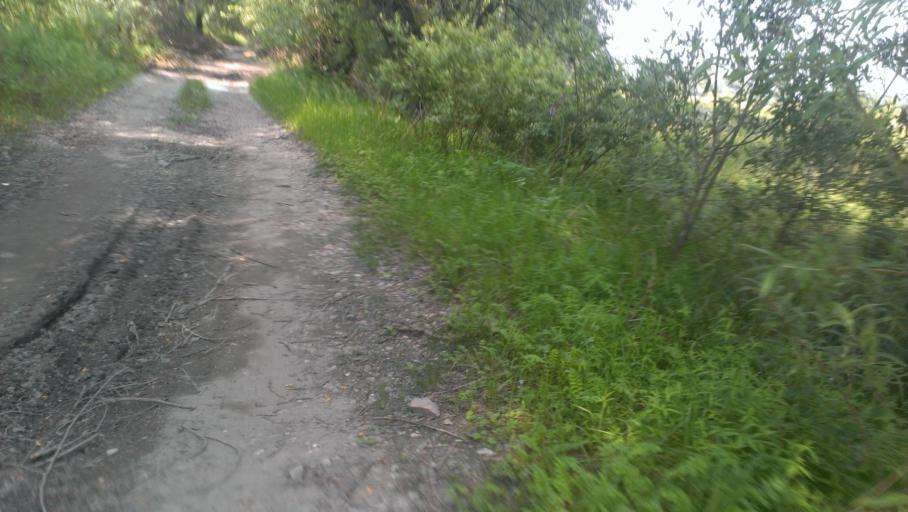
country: RU
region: Altai Krai
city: Novoaltaysk
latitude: 53.3738
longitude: 83.8570
